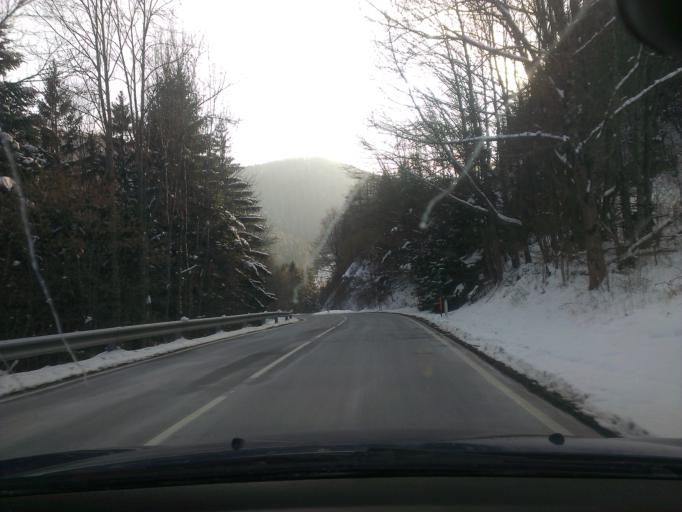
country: AT
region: Lower Austria
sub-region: Politischer Bezirk Wiener Neustadt
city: Miesenbach
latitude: 47.8215
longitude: 15.9544
